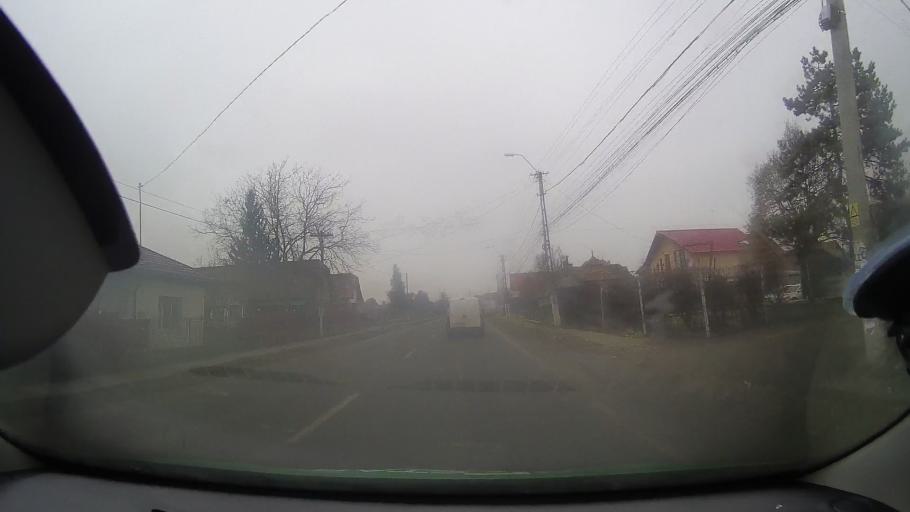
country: RO
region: Cluj
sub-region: Comuna Mihai Viteazu
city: Mihai Viteazu
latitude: 46.5406
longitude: 23.7659
